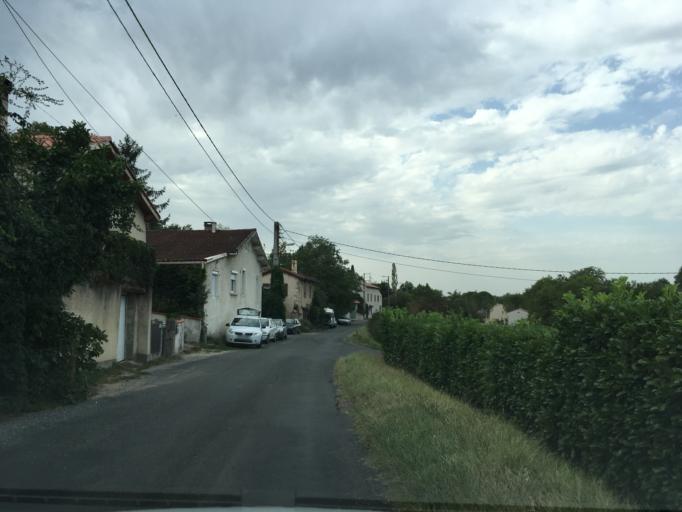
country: FR
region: Midi-Pyrenees
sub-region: Departement du Tarn
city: Castres
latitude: 43.6026
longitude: 2.2725
